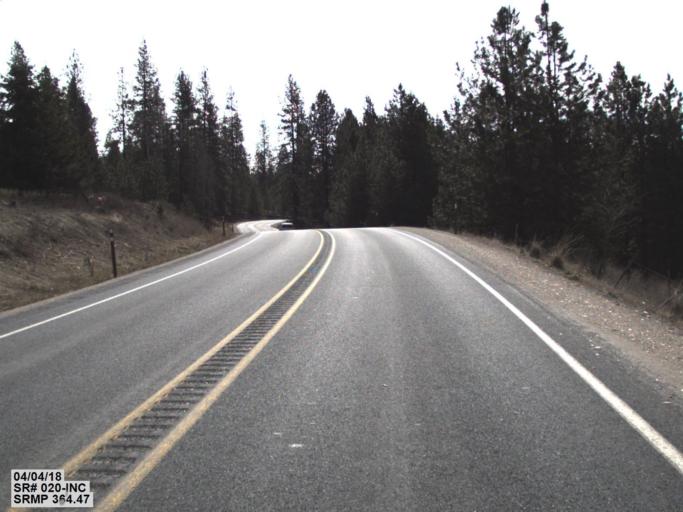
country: US
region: Washington
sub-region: Stevens County
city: Colville
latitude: 48.5086
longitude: -117.7226
